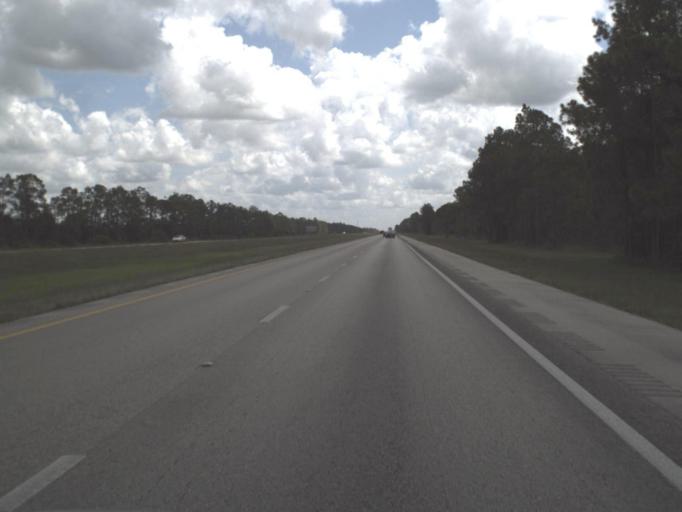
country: US
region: Florida
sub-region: Collier County
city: Golden Gate
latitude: 26.1546
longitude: -81.6397
